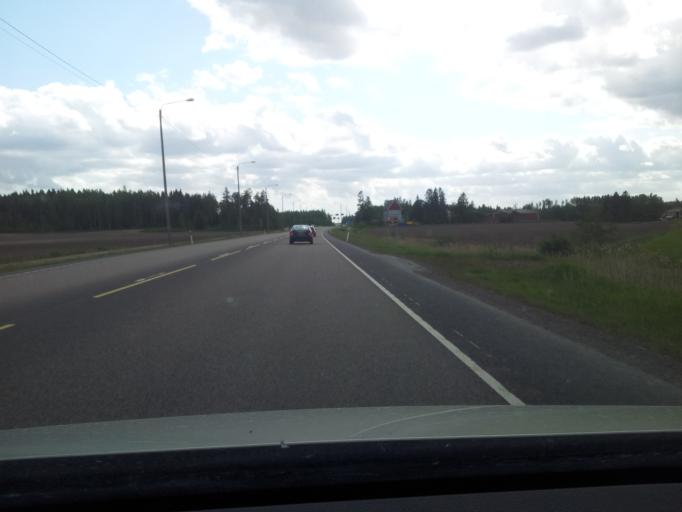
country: FI
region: Kymenlaakso
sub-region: Kouvola
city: Elimaeki
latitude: 60.8205
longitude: 26.5309
